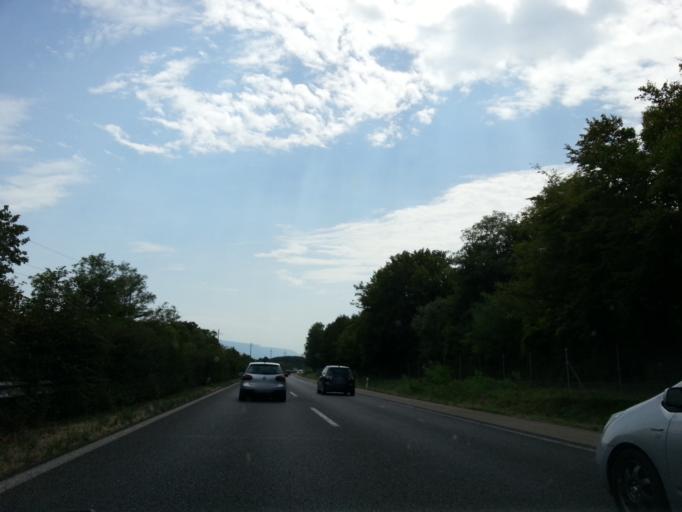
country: CH
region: Geneva
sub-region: Geneva
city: Versoix
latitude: 46.2899
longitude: 6.1460
